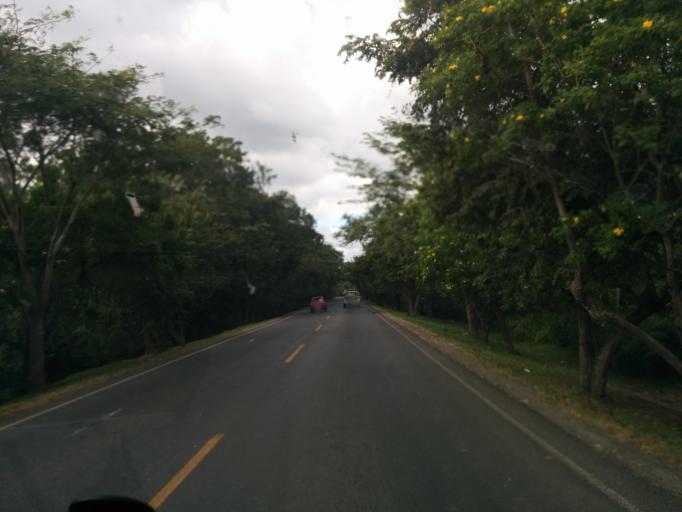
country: NI
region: Esteli
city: Esteli
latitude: 13.1337
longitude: -86.3657
